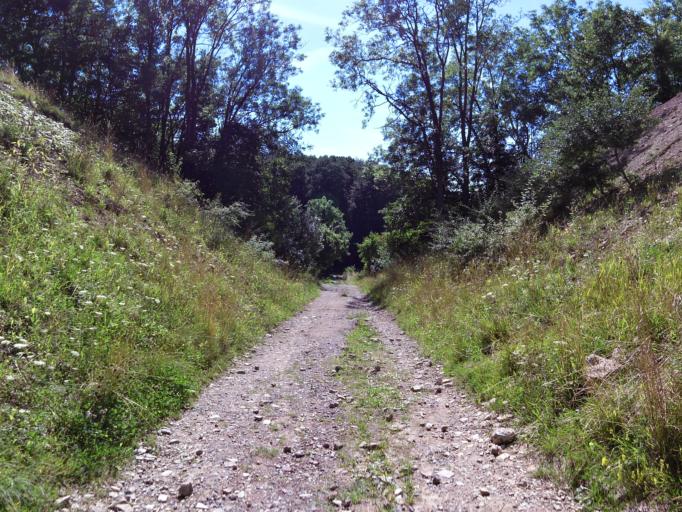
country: DE
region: Thuringia
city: Seebach
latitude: 50.9577
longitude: 10.4482
